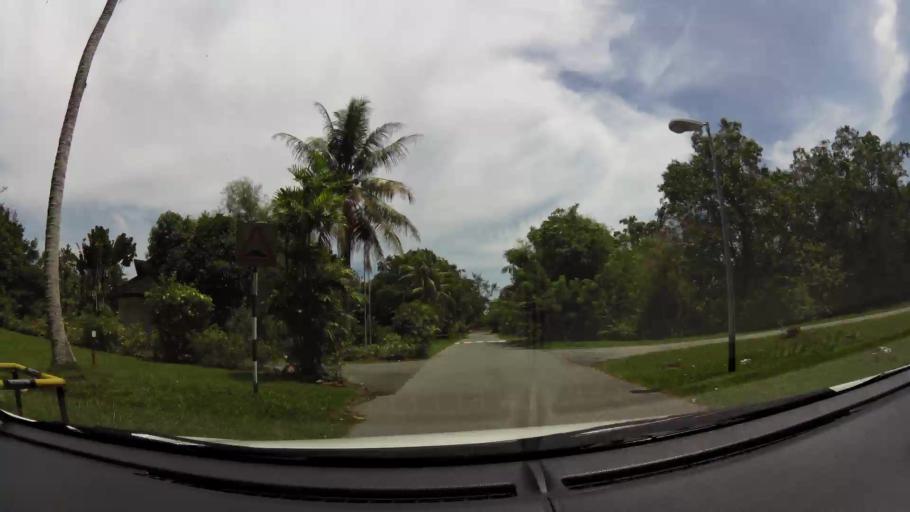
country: BN
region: Belait
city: Kuala Belait
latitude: 4.5949
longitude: 114.2563
